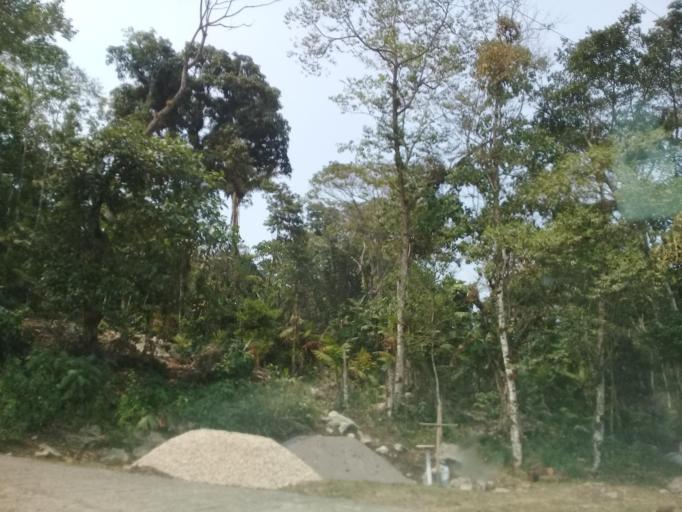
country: MX
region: Veracruz
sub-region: Tezonapa
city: Laguna Chica (Pueblo Nuevo)
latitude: 18.5860
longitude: -96.7460
